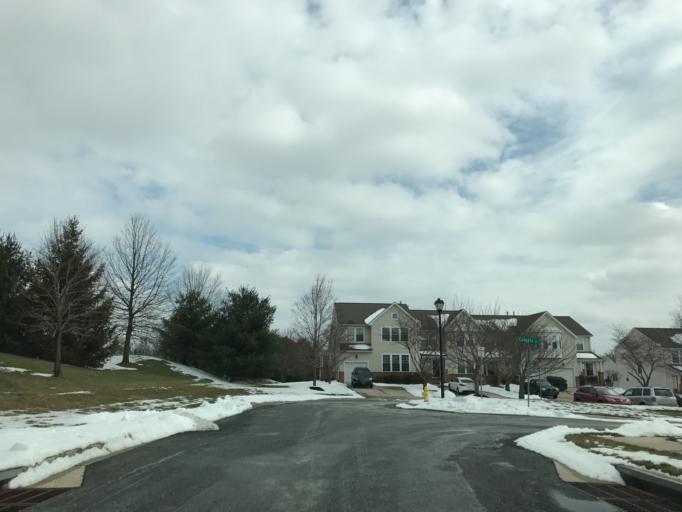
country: US
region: Maryland
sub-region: Harford County
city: Bel Air North
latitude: 39.5755
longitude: -76.3804
